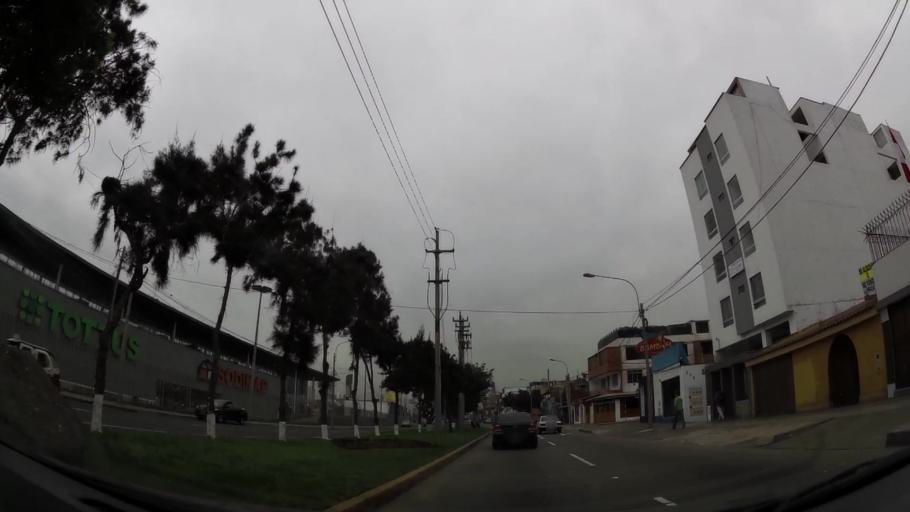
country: PE
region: Callao
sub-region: Callao
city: Callao
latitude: -12.0807
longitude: -77.0882
